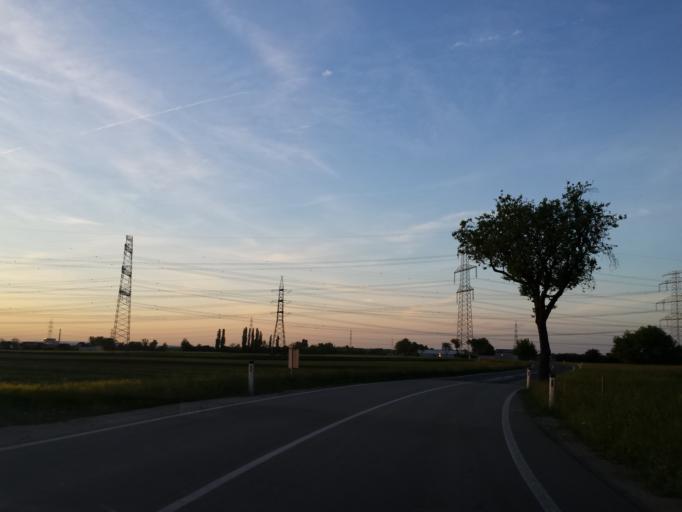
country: AT
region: Lower Austria
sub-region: Politischer Bezirk Tulln
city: Atzenbrugg
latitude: 48.3250
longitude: 15.9081
